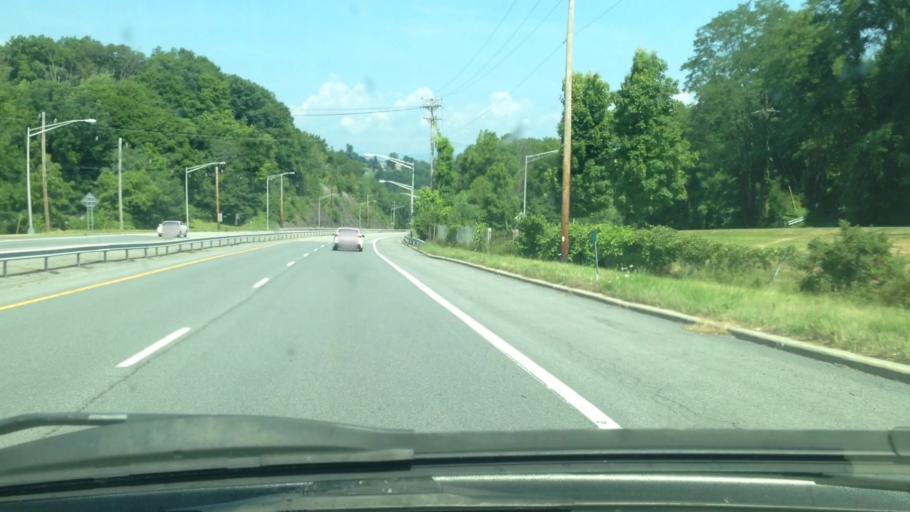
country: US
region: New York
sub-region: Ulster County
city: Port Ewen
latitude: 41.9136
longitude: -73.9782
